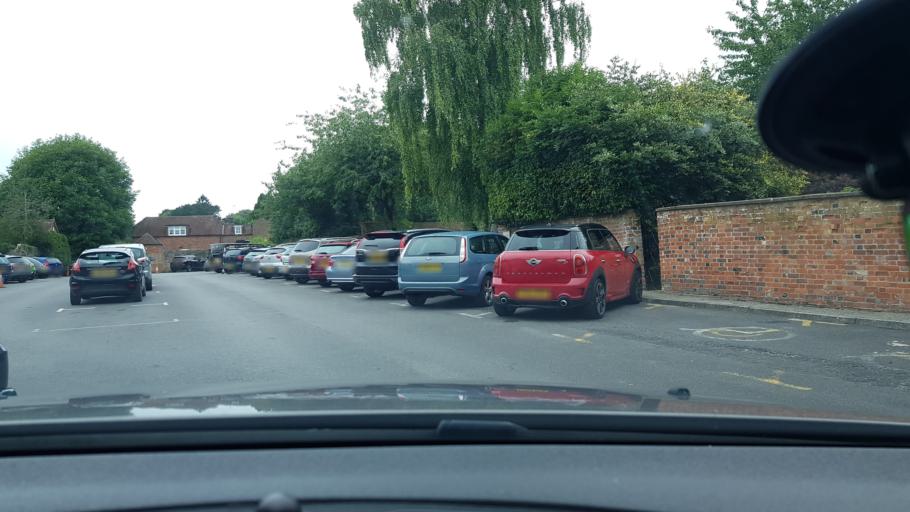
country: GB
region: England
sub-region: Wiltshire
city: Marlborough
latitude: 51.4205
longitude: -1.7321
